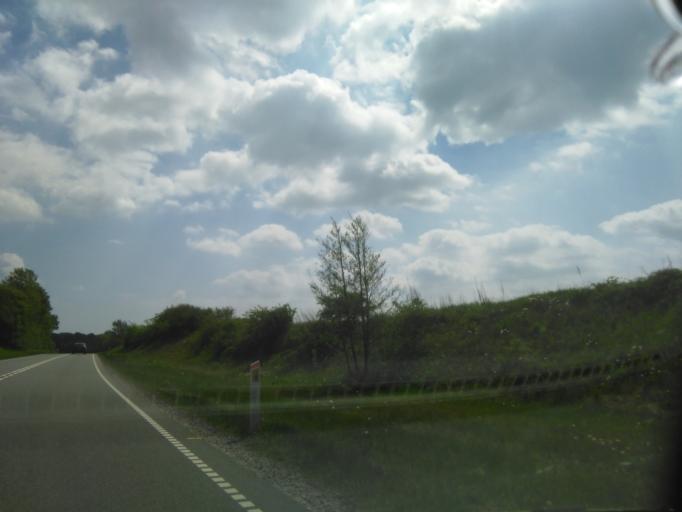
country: DK
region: Central Jutland
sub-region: Skanderborg Kommune
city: Stilling
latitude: 56.0128
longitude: 9.9887
